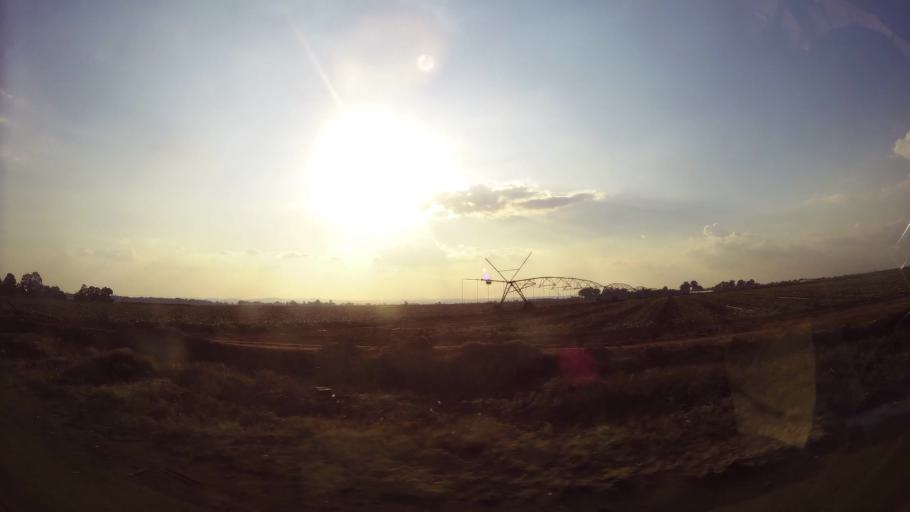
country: ZA
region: Gauteng
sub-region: Ekurhuleni Metropolitan Municipality
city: Germiston
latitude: -26.3268
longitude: 28.2400
